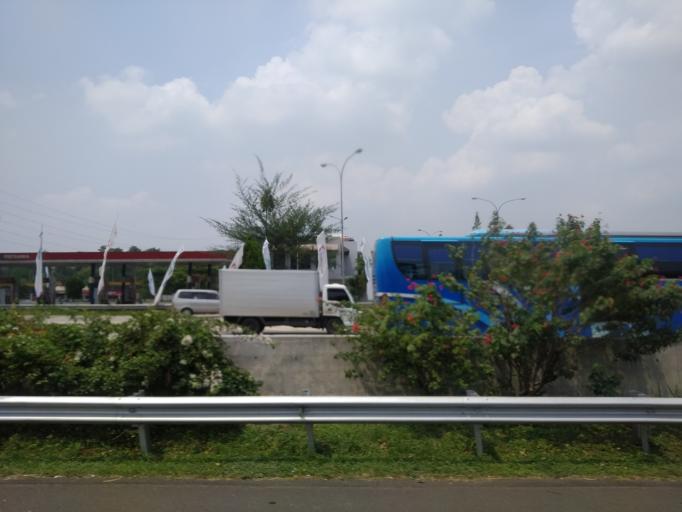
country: ID
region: West Java
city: Citeureup
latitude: -6.4360
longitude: 106.8939
